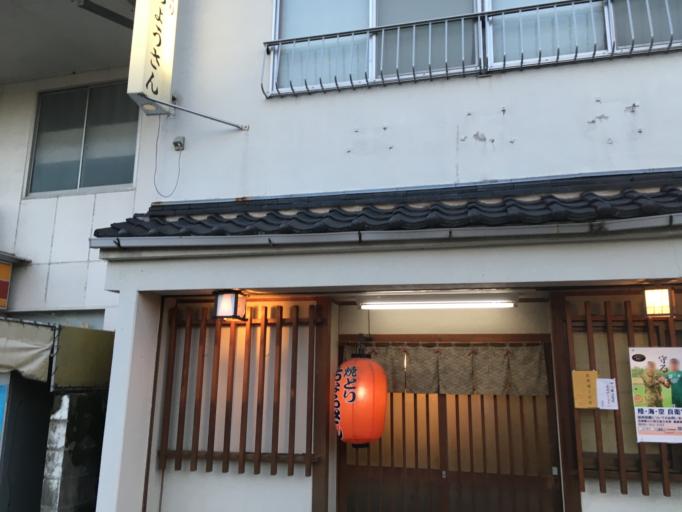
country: JP
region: Yamaguchi
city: Yamaguchi-shi
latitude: 34.1815
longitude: 131.4777
